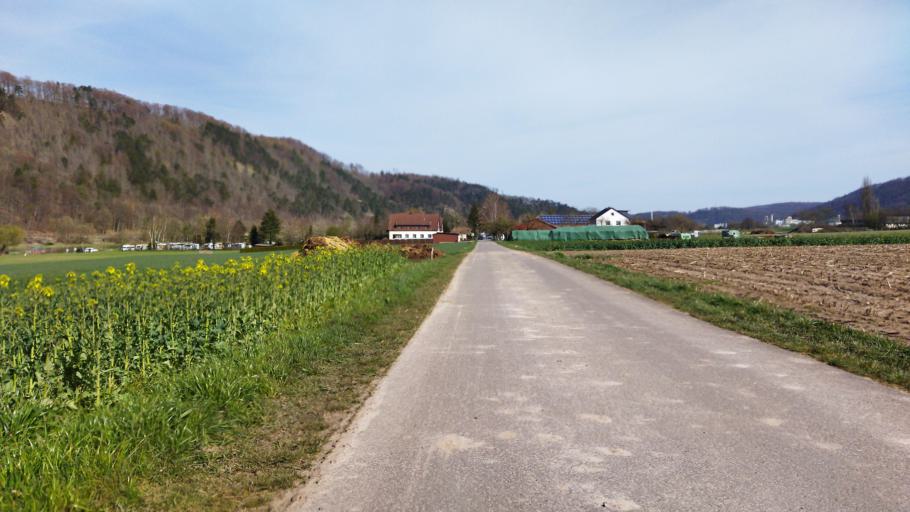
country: DE
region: Lower Saxony
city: Bodenwerder
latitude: 51.9560
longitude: 9.5051
